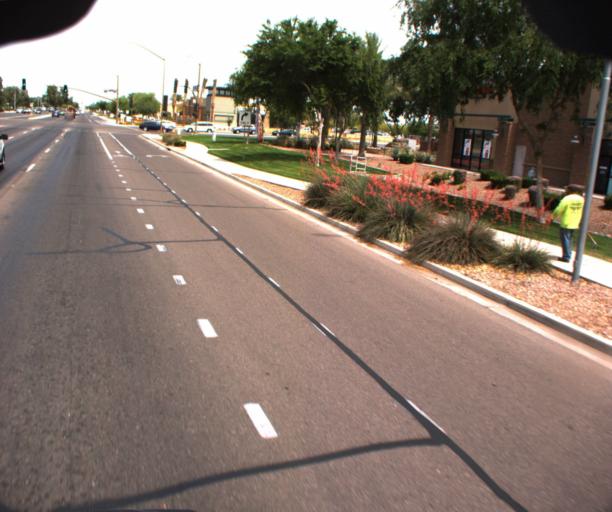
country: US
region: Arizona
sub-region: Maricopa County
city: Sun Lakes
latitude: 33.2468
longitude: -111.8411
